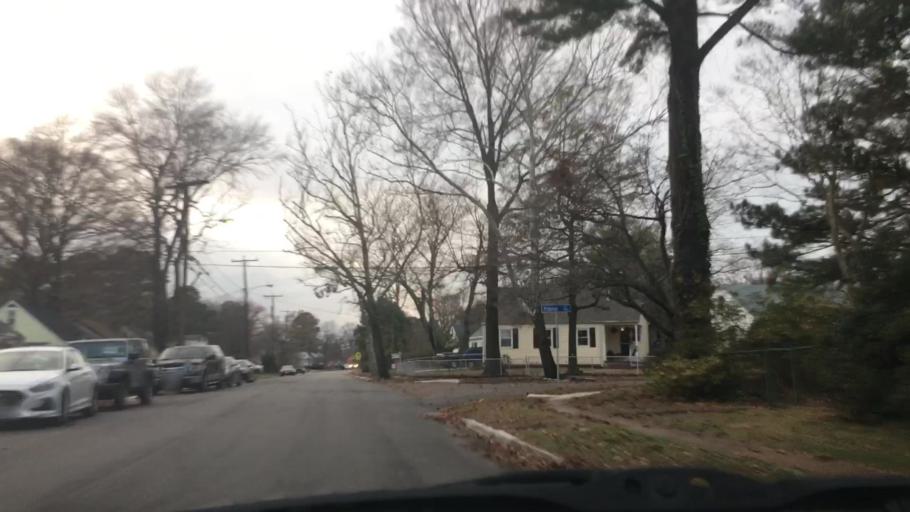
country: US
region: Virginia
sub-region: City of Norfolk
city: Norfolk
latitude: 36.9288
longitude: -76.2358
